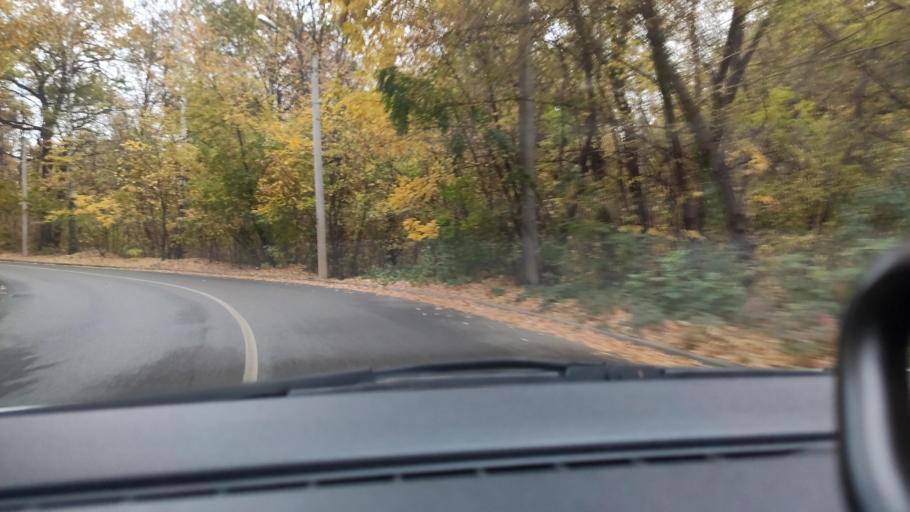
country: RU
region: Voronezj
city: Voronezh
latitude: 51.7189
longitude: 39.2351
